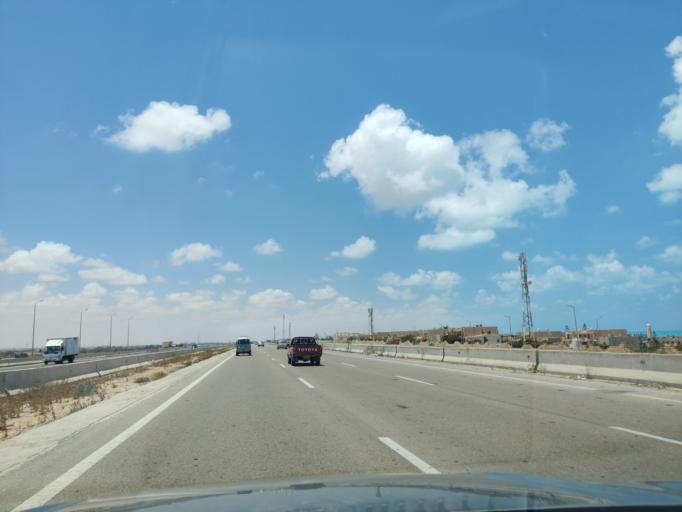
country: EG
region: Muhafazat Matruh
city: Al `Alamayn
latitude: 30.8133
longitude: 29.0549
